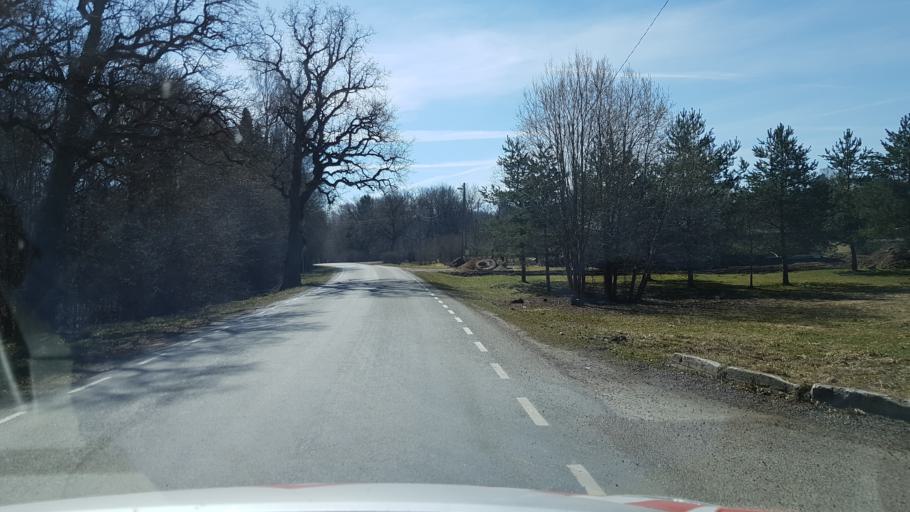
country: EE
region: Laeaene-Virumaa
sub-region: Vinni vald
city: Vinni
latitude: 59.2894
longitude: 26.4268
